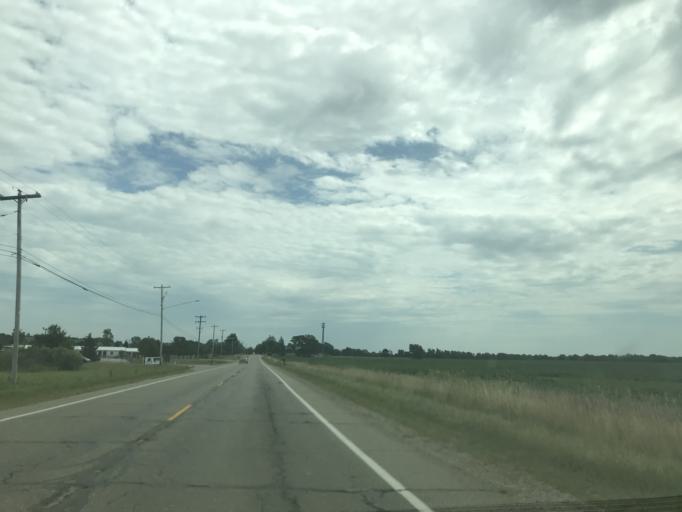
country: US
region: Michigan
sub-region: Clinton County
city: Wacousta
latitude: 42.7961
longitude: -84.7297
